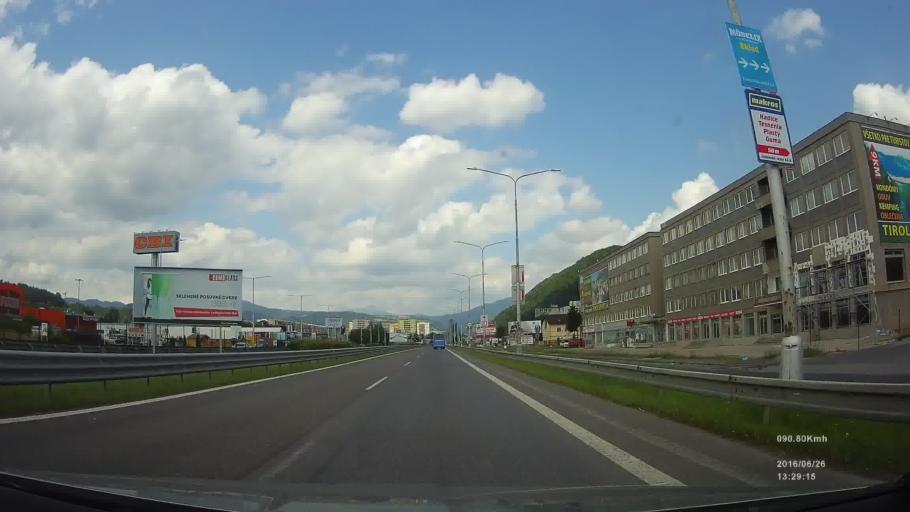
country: SK
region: Banskobystricky
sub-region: Okres Banska Bystrica
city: Banska Bystrica
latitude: 48.7098
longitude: 19.1390
